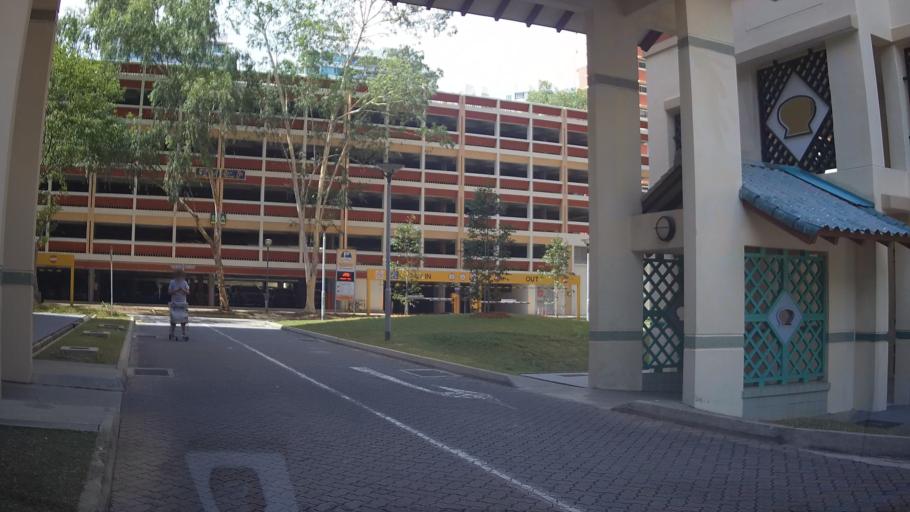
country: MY
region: Johor
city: Kampung Pasir Gudang Baru
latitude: 1.3744
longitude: 103.9443
